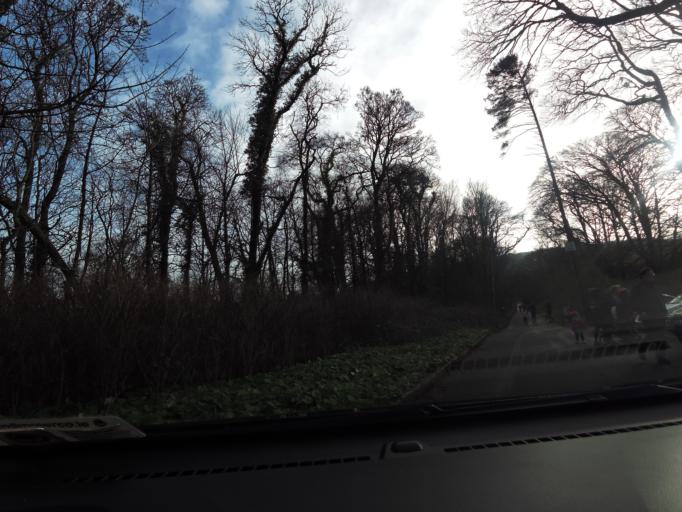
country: IE
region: Connaught
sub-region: County Galway
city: Tuam
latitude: 53.4908
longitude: -8.9708
